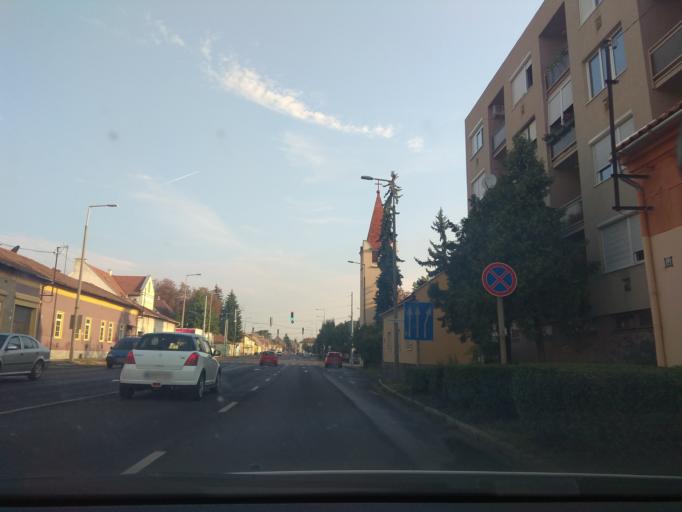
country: HU
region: Heves
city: Eger
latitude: 47.8983
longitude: 20.3676
